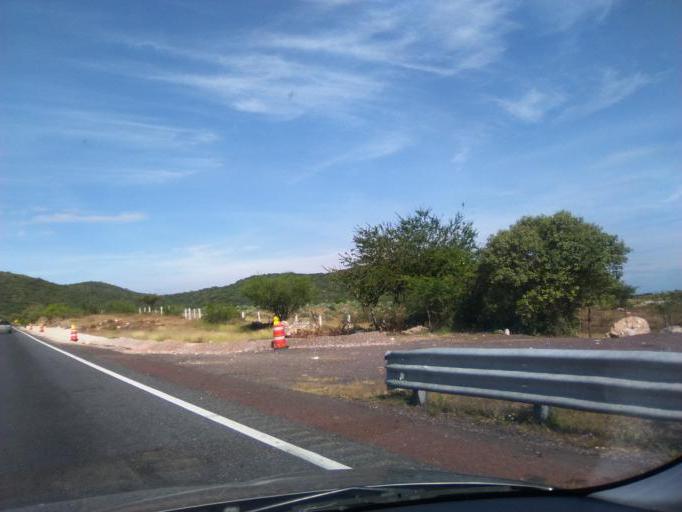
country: MX
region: Guerrero
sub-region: Huitzuco de los Figueroa
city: Ciudad de Huitzuco
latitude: 18.2608
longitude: -99.2109
